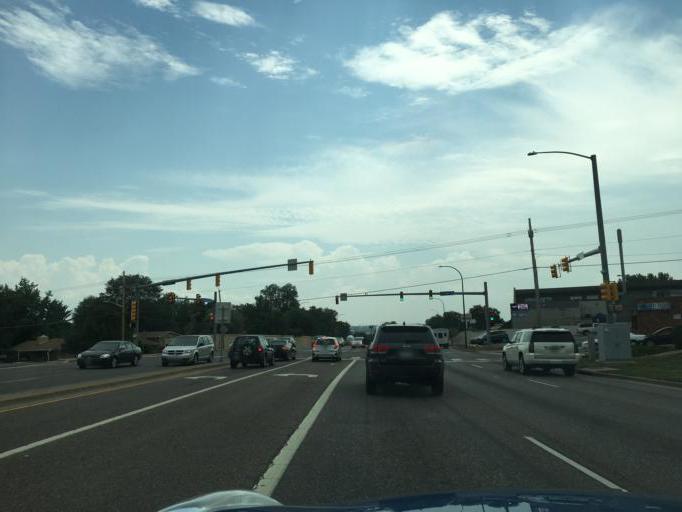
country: US
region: Colorado
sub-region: Jefferson County
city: Arvada
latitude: 39.8135
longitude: -105.0808
